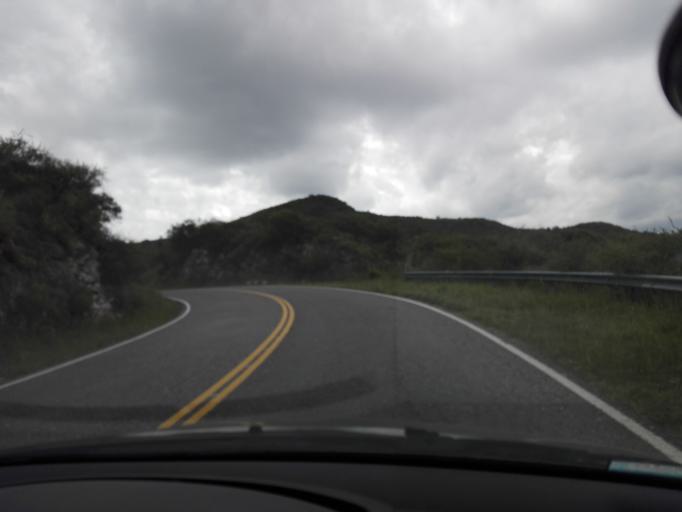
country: AR
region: Cordoba
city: Alta Gracia
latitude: -31.5905
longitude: -64.5164
